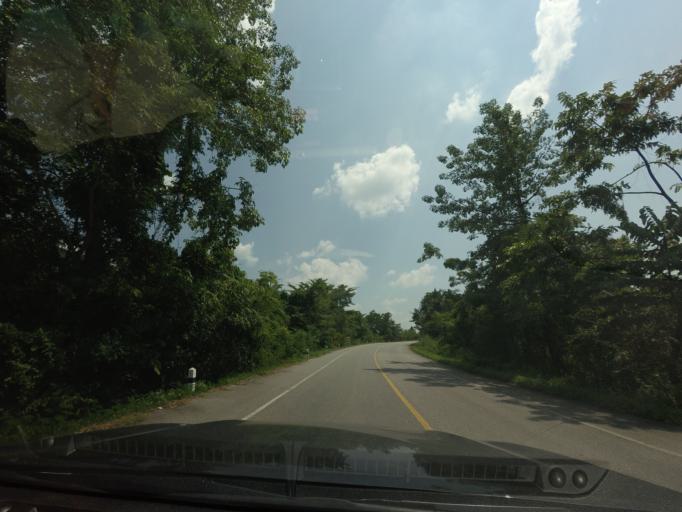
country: TH
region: Uttaradit
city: Thong Saen Khan
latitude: 17.3220
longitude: 100.3877
